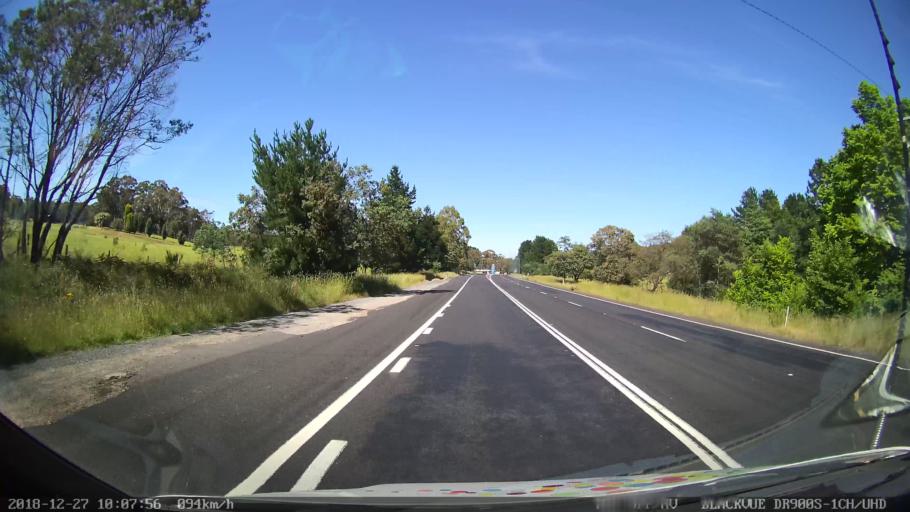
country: AU
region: New South Wales
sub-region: Lithgow
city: Portland
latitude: -33.4442
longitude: 149.8329
